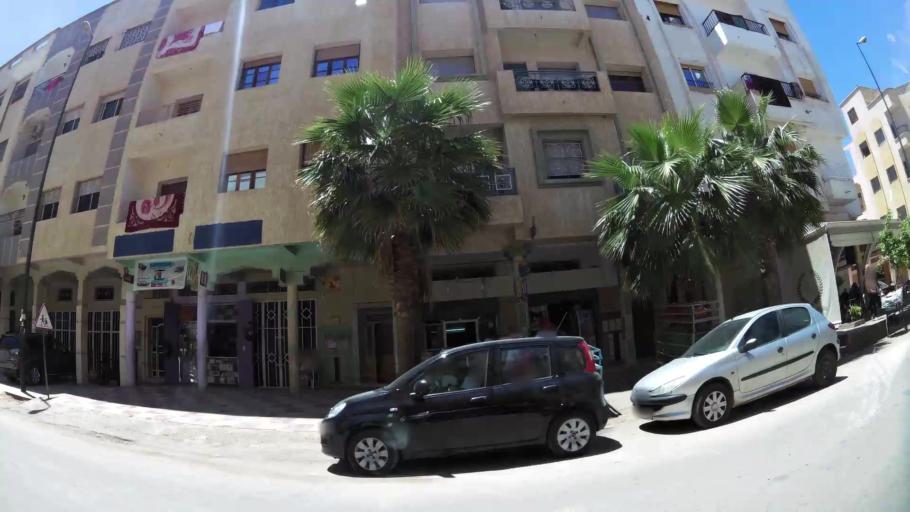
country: MA
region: Meknes-Tafilalet
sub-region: Meknes
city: Meknes
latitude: 33.8605
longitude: -5.5739
